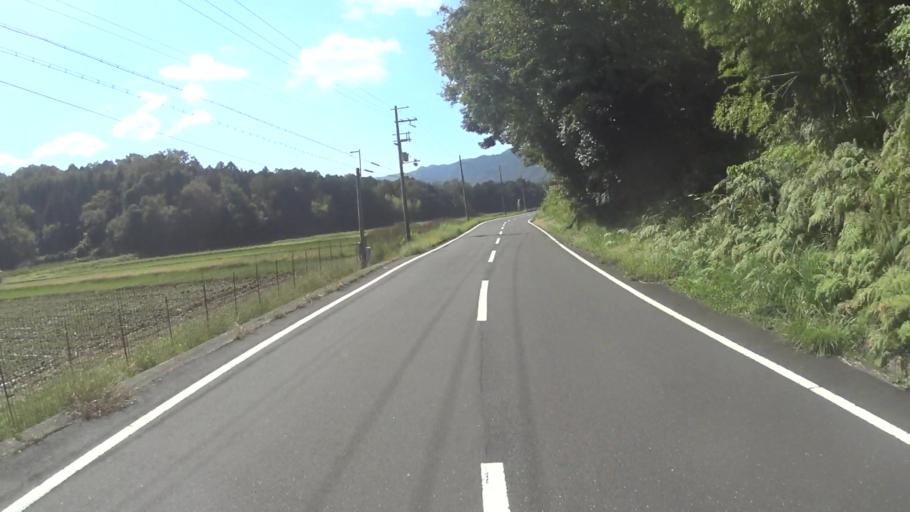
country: JP
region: Hyogo
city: Toyooka
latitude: 35.5833
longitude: 134.9442
